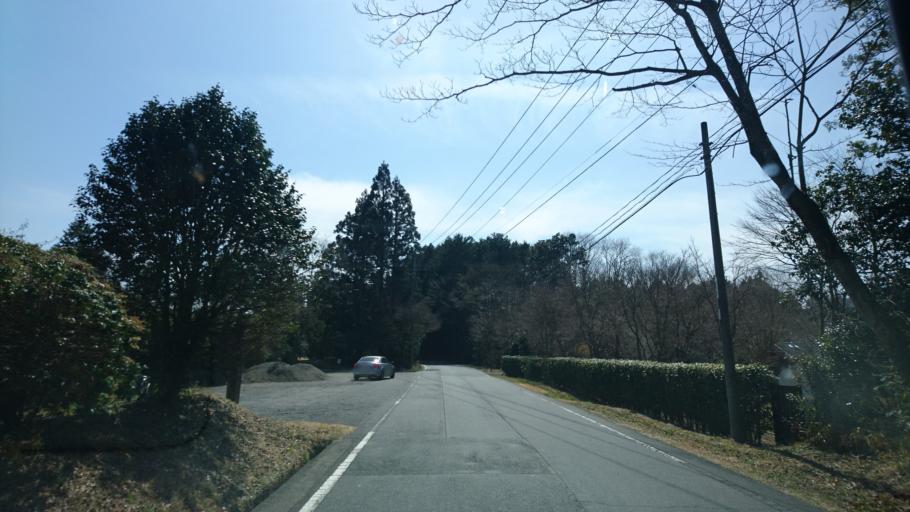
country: JP
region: Shizuoka
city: Fujinomiya
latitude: 35.3541
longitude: 138.5716
